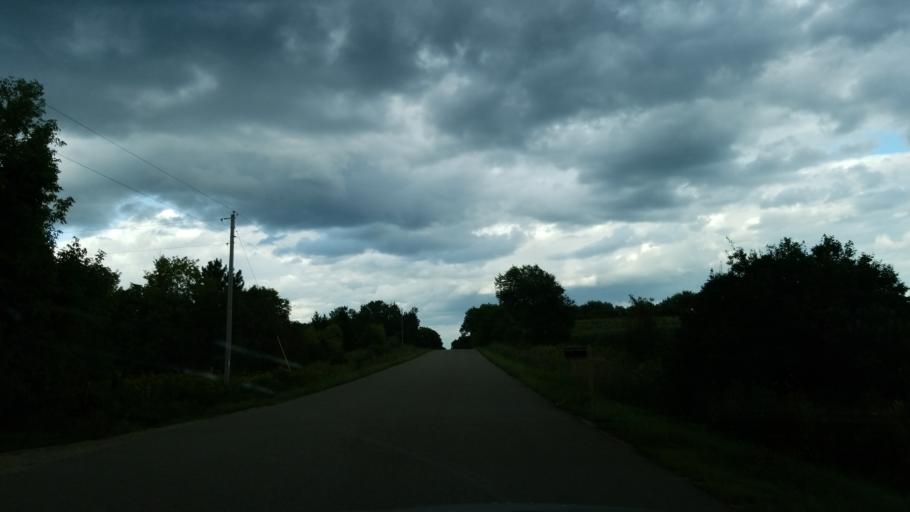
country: US
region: Minnesota
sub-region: Washington County
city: Afton
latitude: 44.8802
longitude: -92.7452
